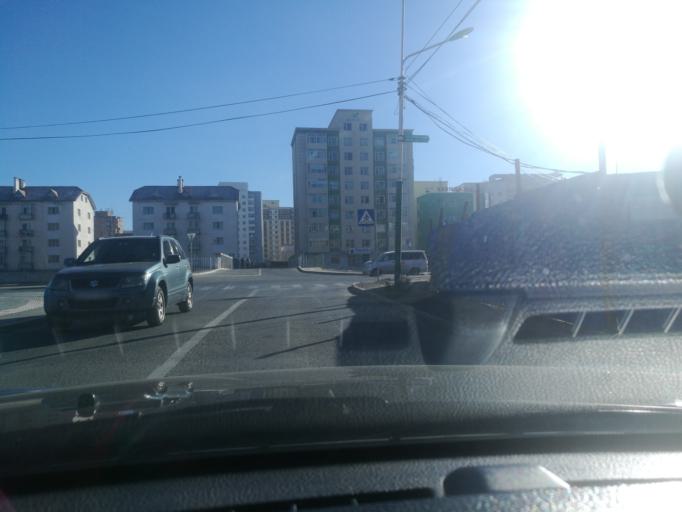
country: MN
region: Ulaanbaatar
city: Ulaanbaatar
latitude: 47.9147
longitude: 106.9290
